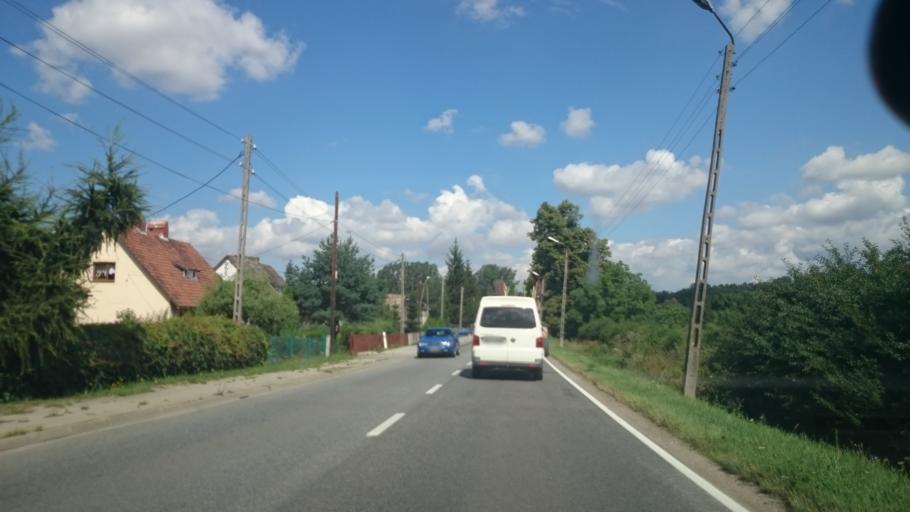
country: PL
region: Lower Silesian Voivodeship
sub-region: Powiat zabkowicki
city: Kamieniec Zabkowicki
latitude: 50.5290
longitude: 16.8669
